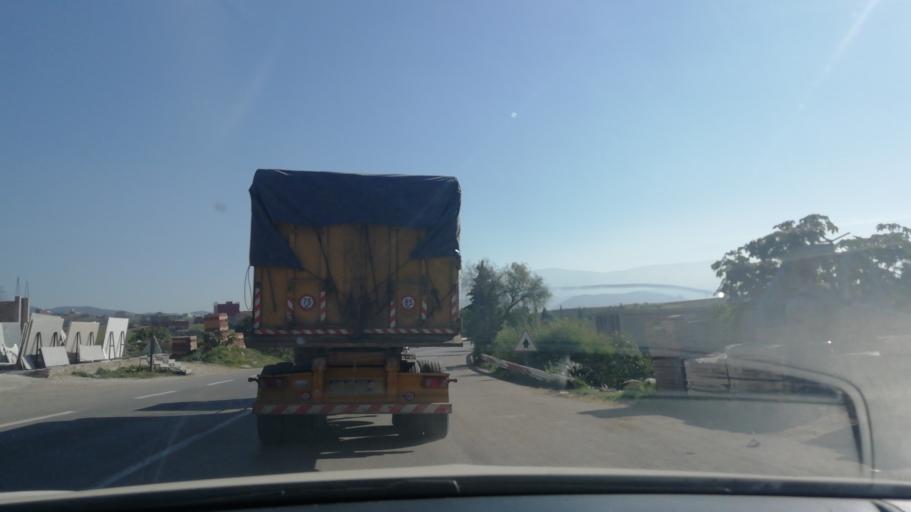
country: DZ
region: Tlemcen
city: Nedroma
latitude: 35.0752
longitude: -1.7797
